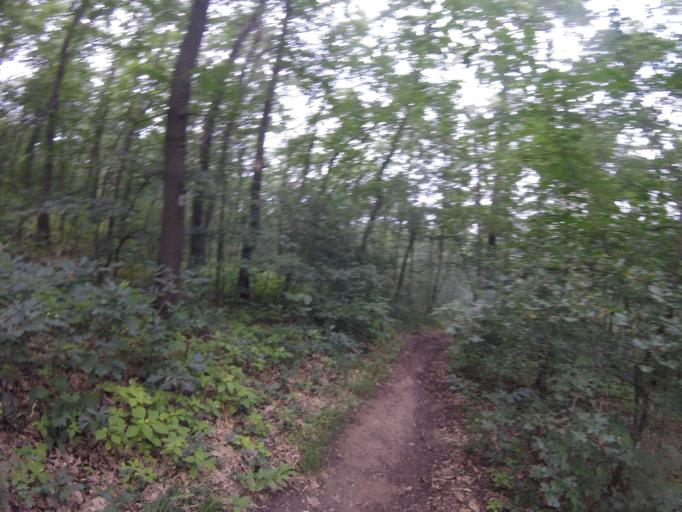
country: HU
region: Pest
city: Toeroekbalint
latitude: 47.4256
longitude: 18.9257
